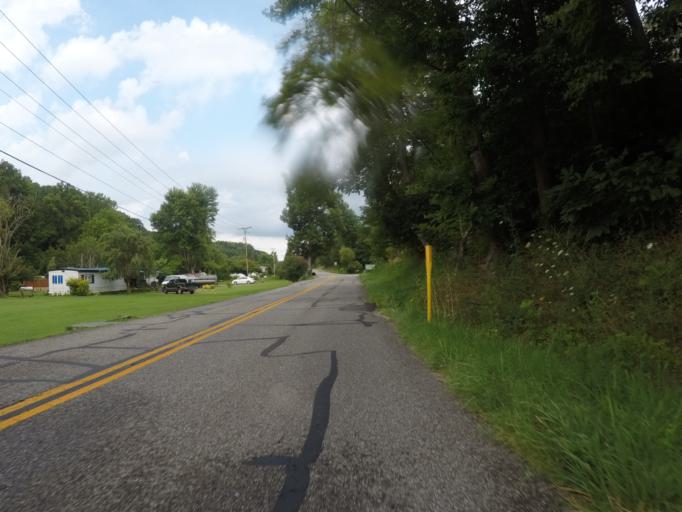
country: US
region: Kentucky
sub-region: Boyd County
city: Meads
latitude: 38.4074
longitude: -82.6632
